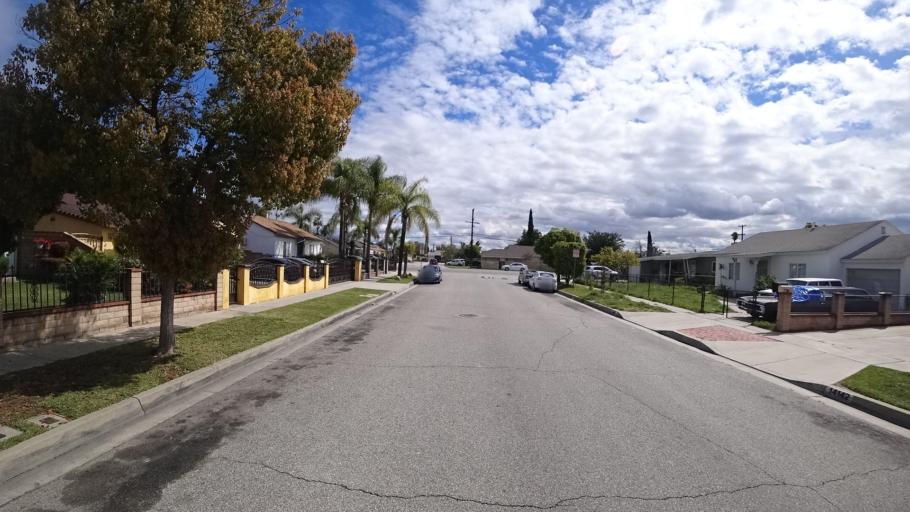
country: US
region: California
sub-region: Los Angeles County
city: Baldwin Park
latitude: 34.0946
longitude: -117.9656
